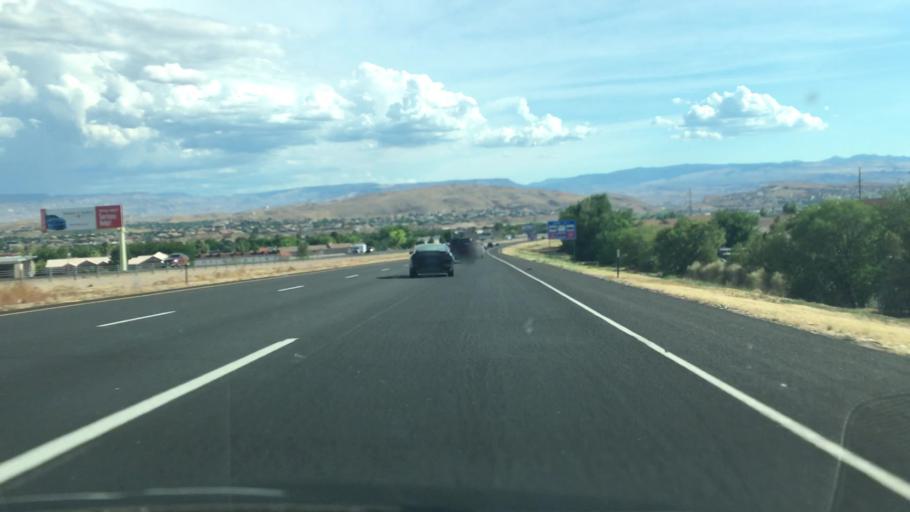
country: US
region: Utah
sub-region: Washington County
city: Saint George
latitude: 37.1052
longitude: -113.5605
